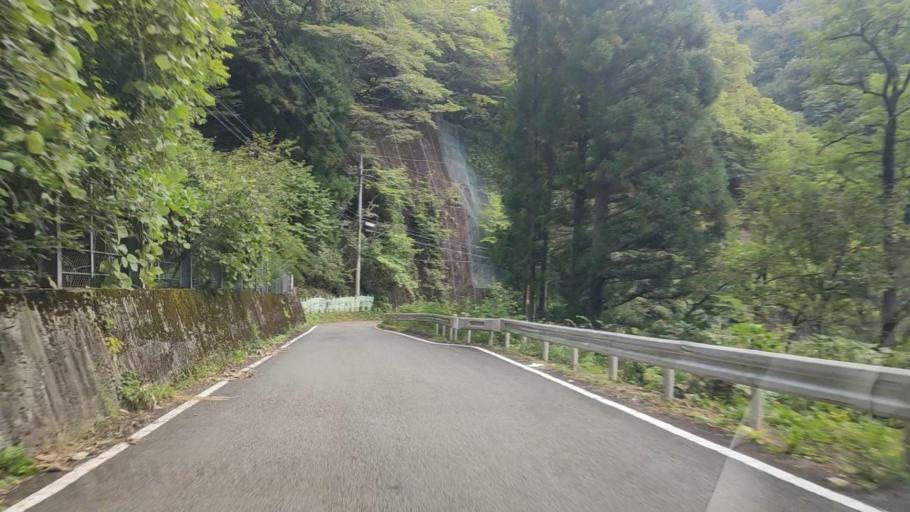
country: JP
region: Gunma
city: Nakanojomachi
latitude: 36.6497
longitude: 138.6410
